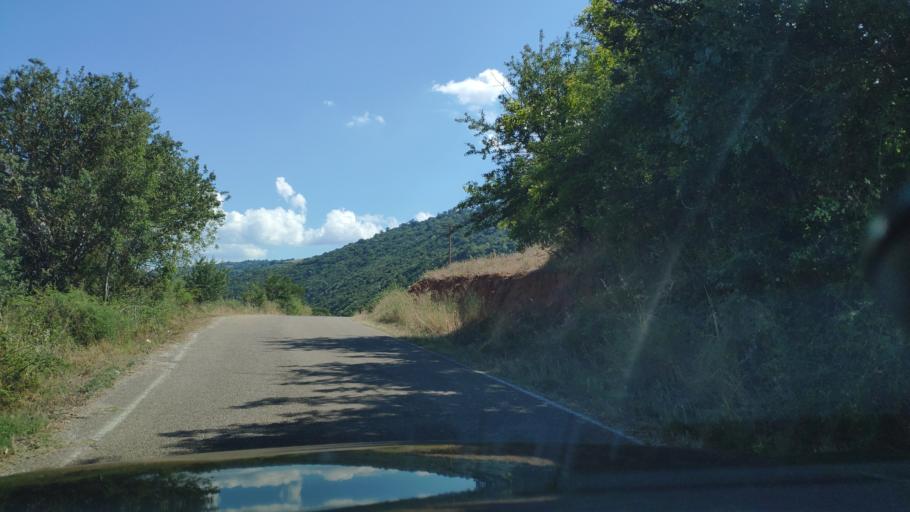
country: GR
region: West Greece
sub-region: Nomos Aitolias kai Akarnanias
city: Katouna
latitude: 38.8350
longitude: 21.0994
